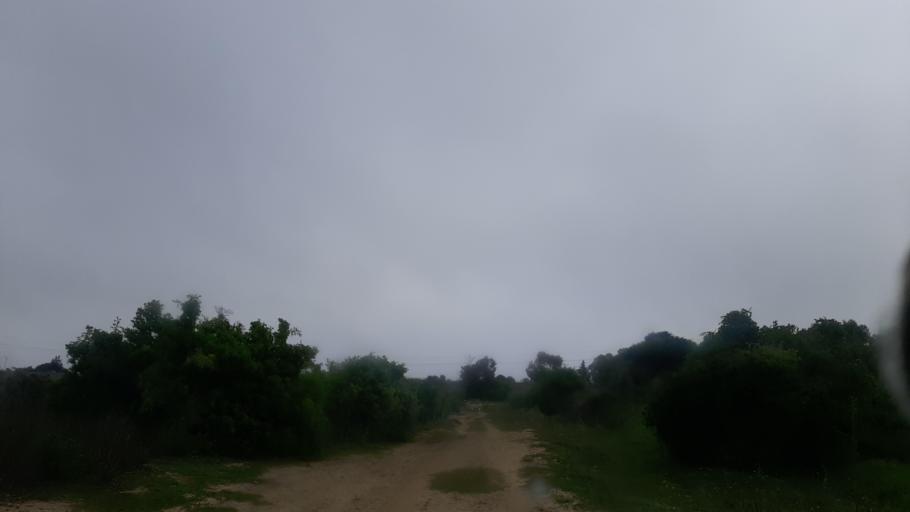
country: TN
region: Nabul
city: Qulaybiyah
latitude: 36.8234
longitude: 11.0458
